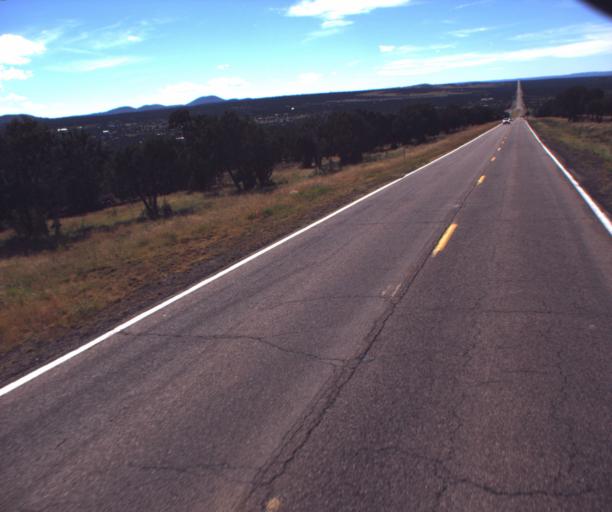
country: US
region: Arizona
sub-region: Navajo County
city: White Mountain Lake
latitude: 34.2886
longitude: -109.8216
